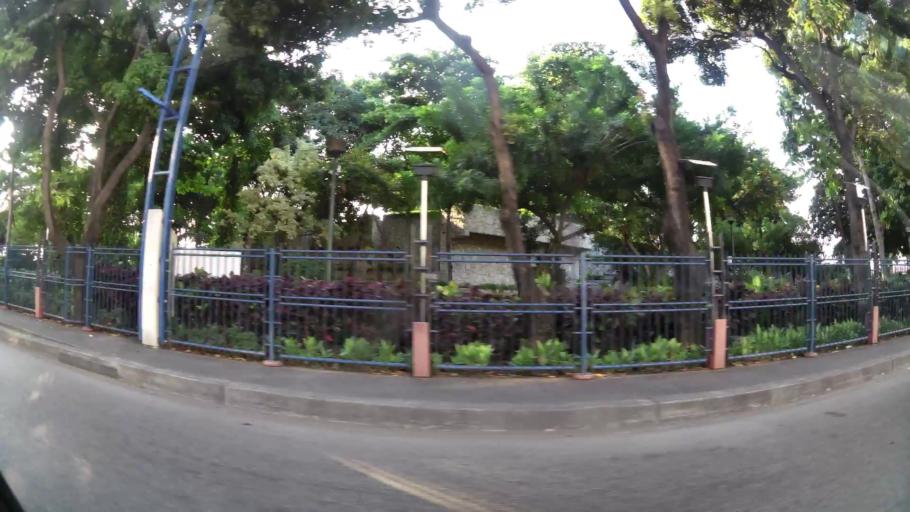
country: EC
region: Guayas
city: Eloy Alfaro
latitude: -2.1872
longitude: -79.8776
